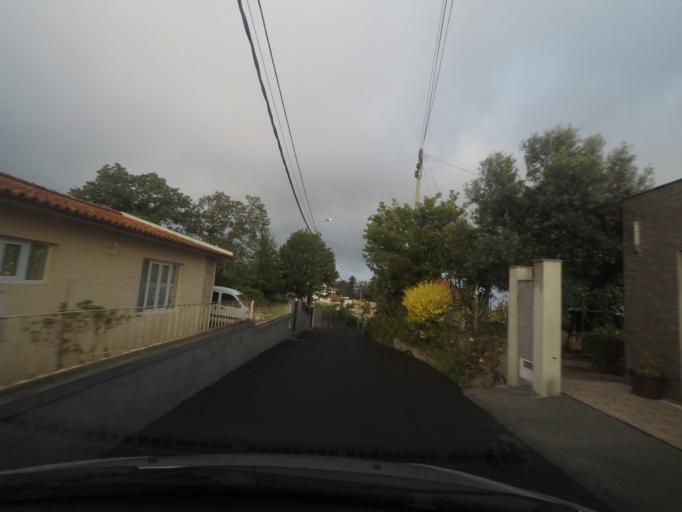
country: PT
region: Madeira
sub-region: Santa Cruz
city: Camacha
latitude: 32.6799
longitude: -16.8495
